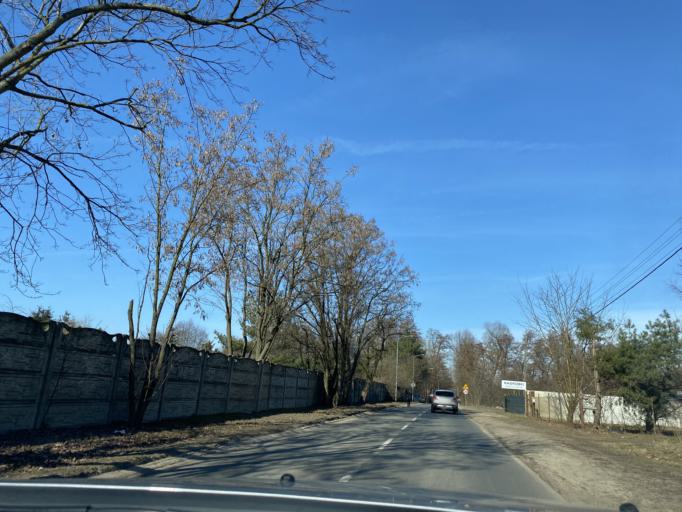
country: PL
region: Greater Poland Voivodeship
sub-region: Powiat poznanski
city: Plewiska
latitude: 52.4024
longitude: 16.8208
